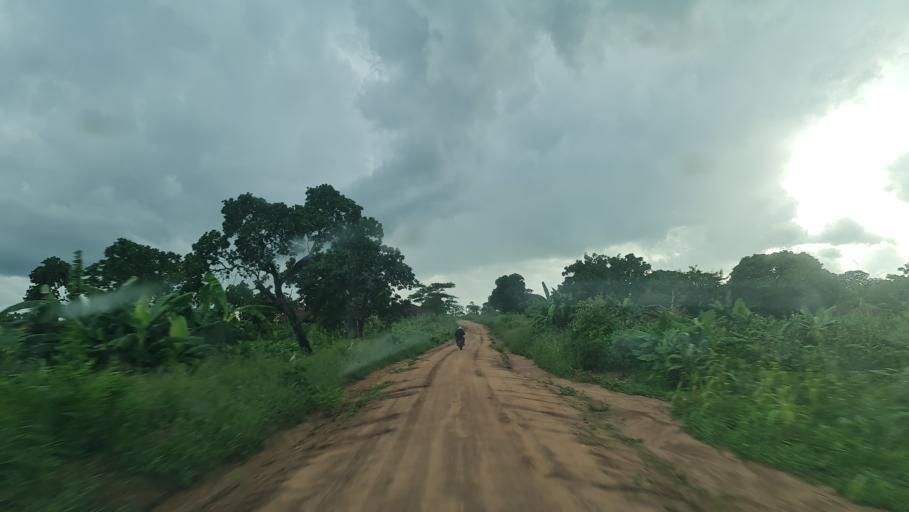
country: MZ
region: Nampula
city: Nacala
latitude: -13.9923
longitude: 40.3685
